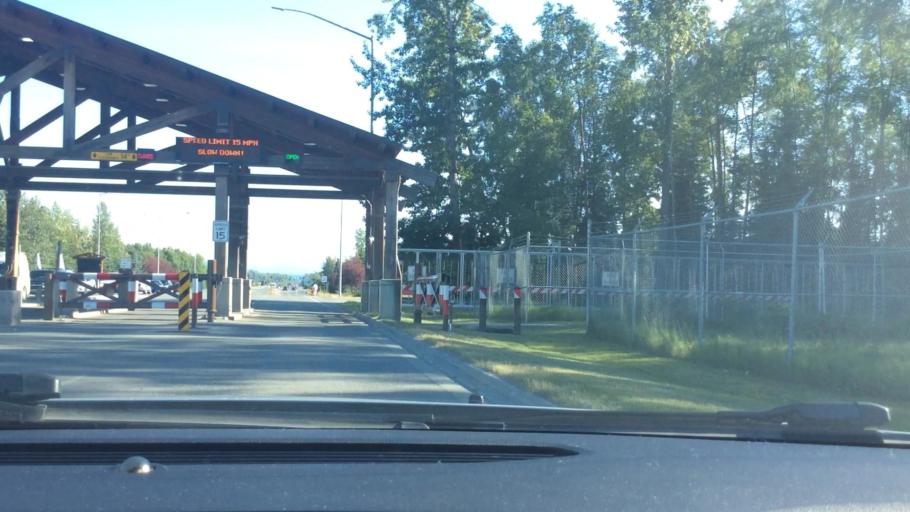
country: US
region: Alaska
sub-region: Anchorage Municipality
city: Anchorage
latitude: 61.2309
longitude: -149.7787
